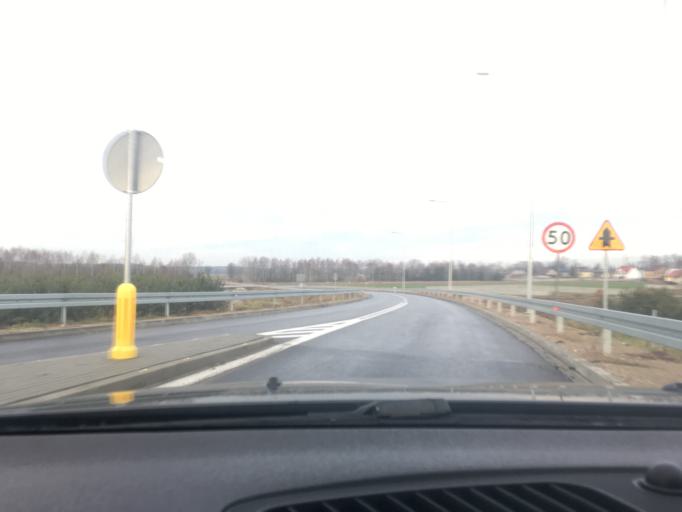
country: PL
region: Swietokrzyskie
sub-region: Powiat jedrzejowski
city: Sobkow
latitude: 50.6916
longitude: 20.3692
